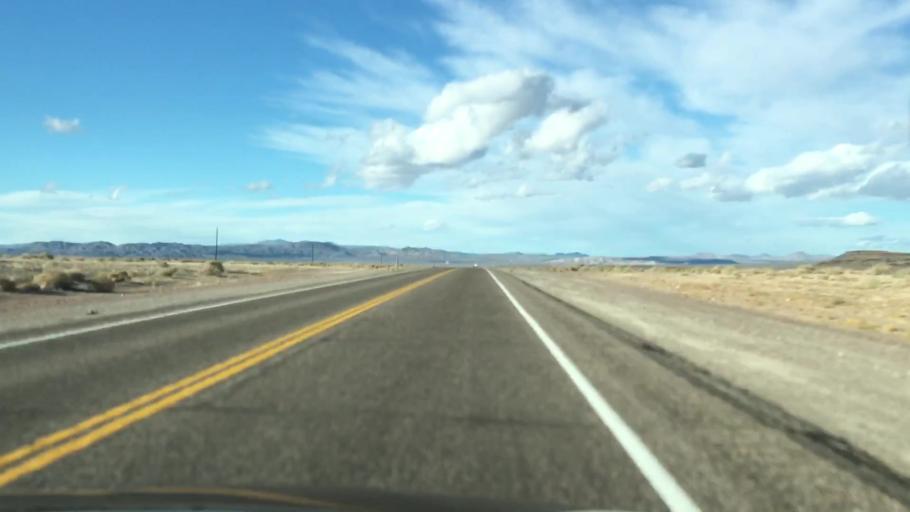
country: US
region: Nevada
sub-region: Esmeralda County
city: Goldfield
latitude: 37.3895
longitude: -117.1444
